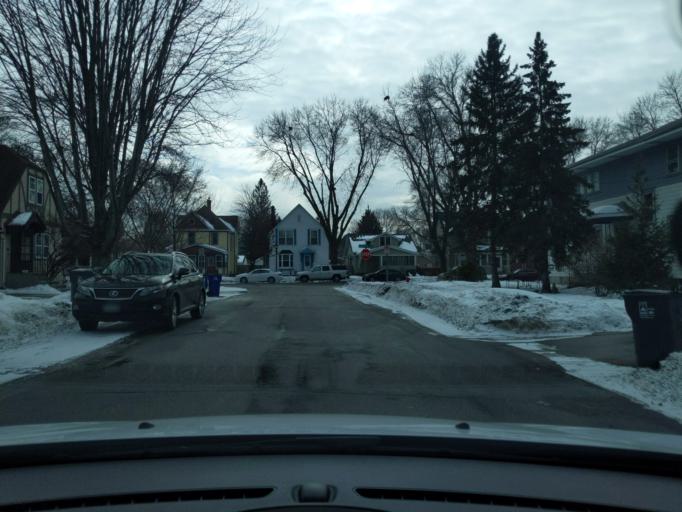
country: US
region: Minnesota
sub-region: Ramsey County
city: Falcon Heights
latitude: 44.9634
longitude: -93.1607
